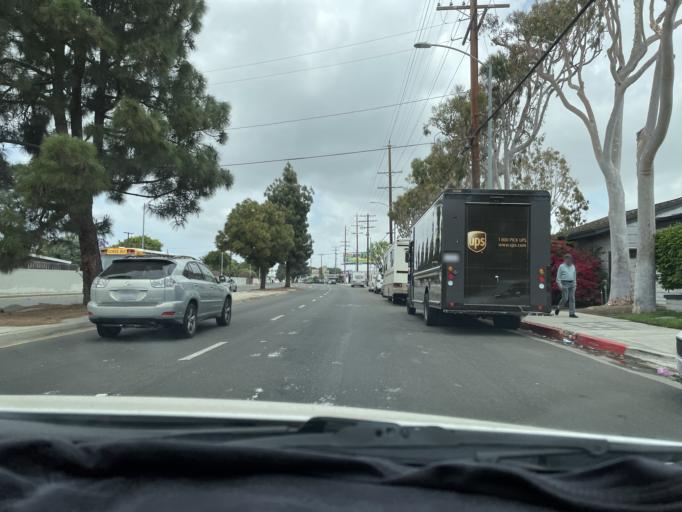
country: US
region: California
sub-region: Los Angeles County
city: Lomita
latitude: 33.8059
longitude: -118.3074
